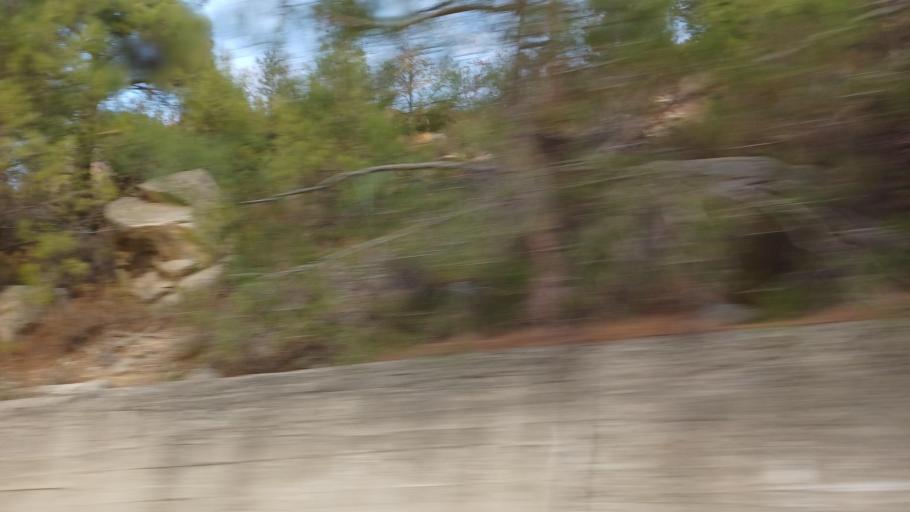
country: CY
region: Lefkosia
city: Kakopetria
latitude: 34.9813
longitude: 32.9083
